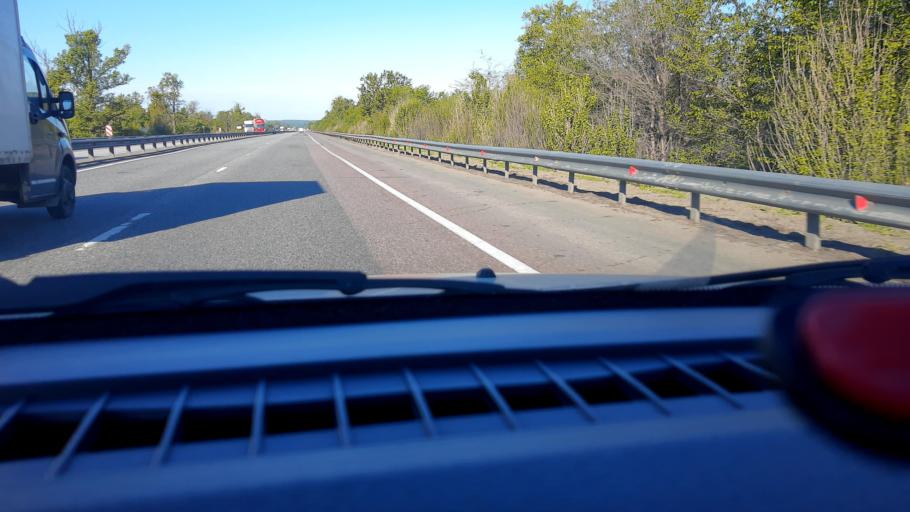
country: RU
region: Vladimir
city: Gorokhovets
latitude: 56.2167
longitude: 42.7606
